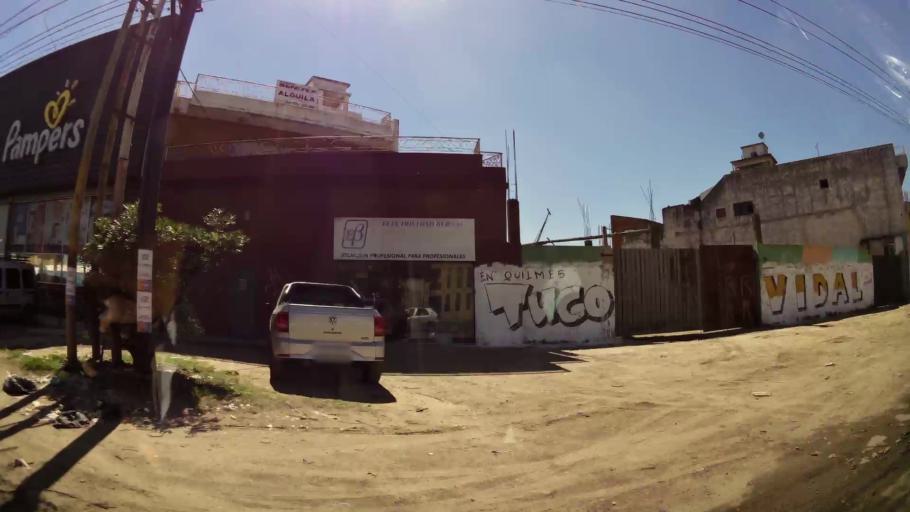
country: AR
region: Buenos Aires
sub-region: Partido de Quilmes
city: Quilmes
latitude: -34.7220
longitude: -58.3030
